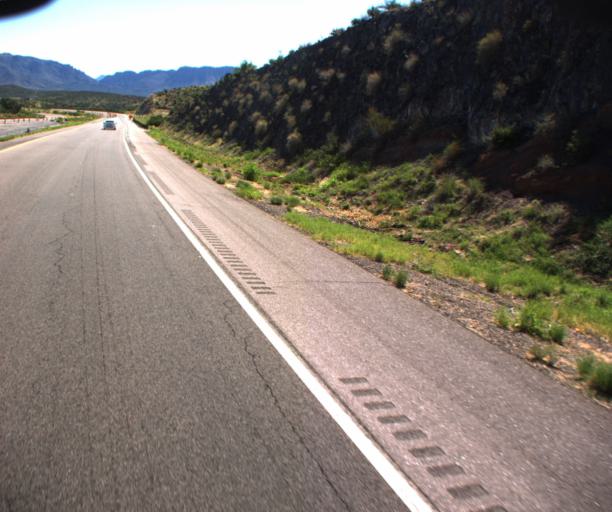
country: US
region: Arizona
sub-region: Pinal County
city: Superior
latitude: 33.2757
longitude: -111.1802
